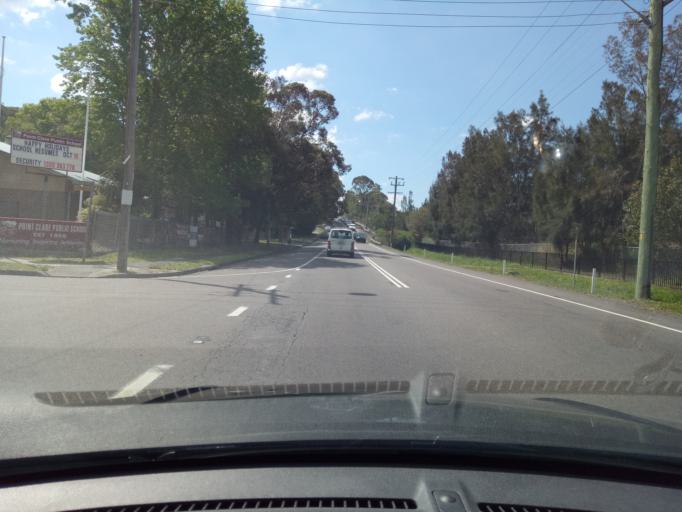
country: AU
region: New South Wales
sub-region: Gosford Shire
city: Point Clare
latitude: -33.4442
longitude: 151.3287
